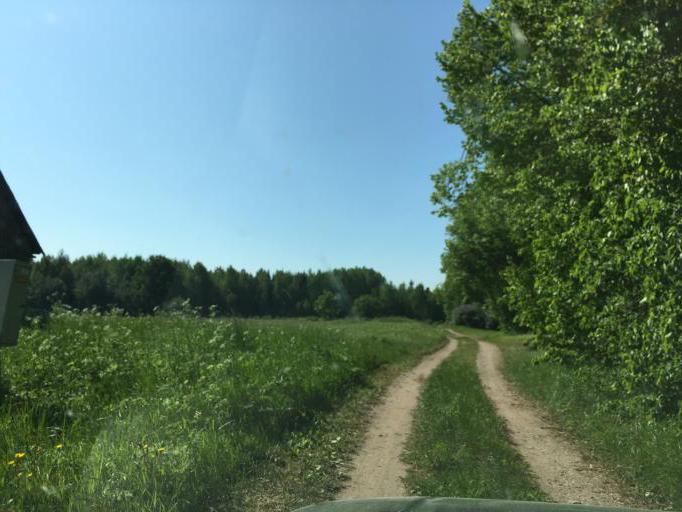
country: LV
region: Ventspils
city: Ventspils
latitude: 57.4814
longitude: 21.7628
